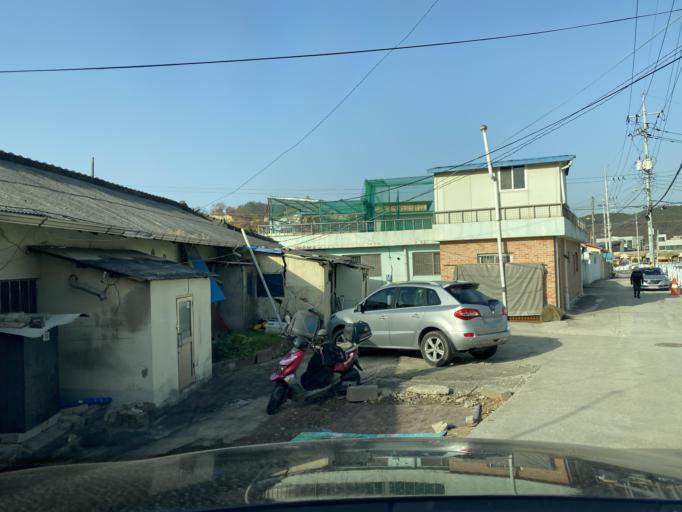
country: KR
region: Chungcheongnam-do
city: Yesan
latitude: 36.6752
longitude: 126.8498
